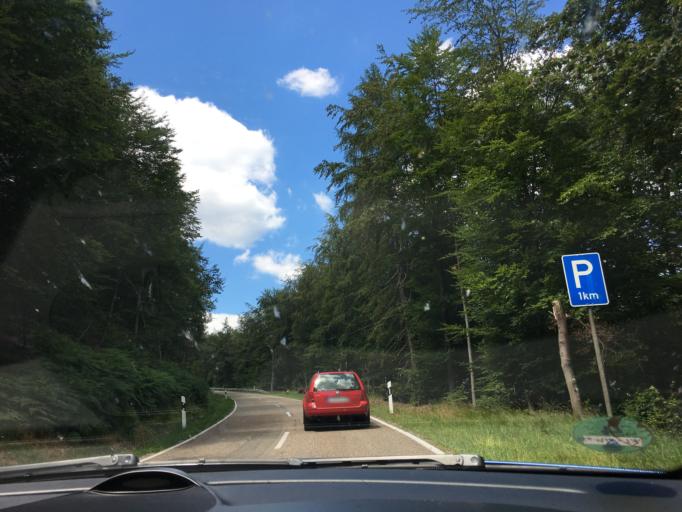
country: DE
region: Rheinland-Pfalz
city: Hauenstein
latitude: 49.2313
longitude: 7.8440
